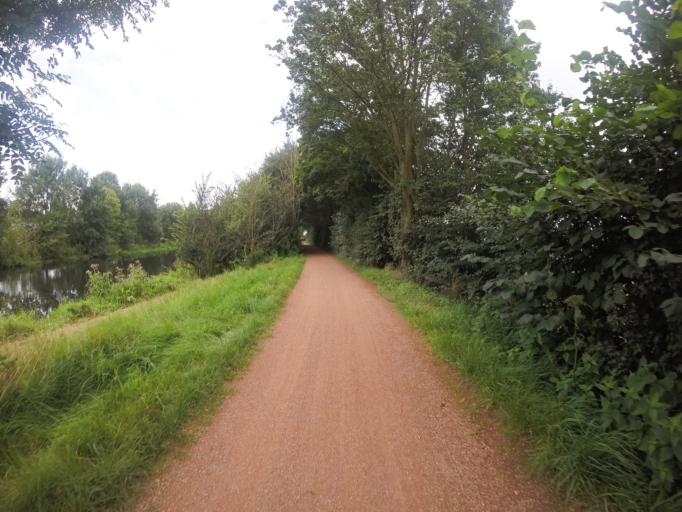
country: DE
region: North Rhine-Westphalia
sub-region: Regierungsbezirk Dusseldorf
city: Bocholt
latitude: 51.8435
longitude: 6.5687
